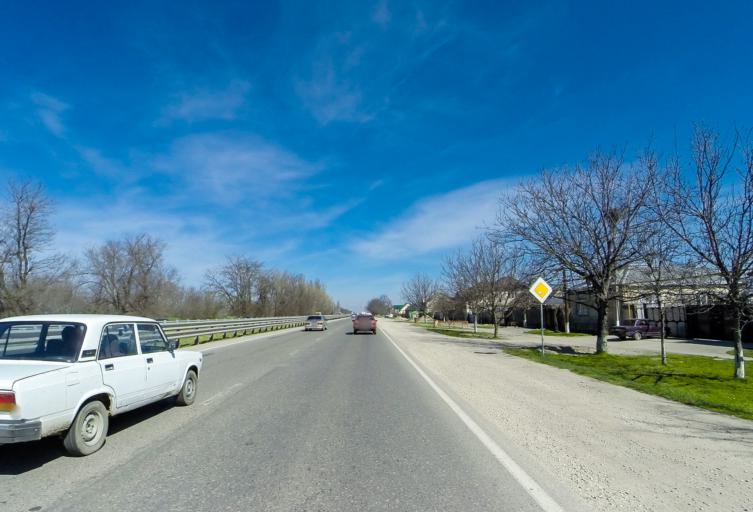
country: RU
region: Kabardino-Balkariya
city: Chegem Vtoroy
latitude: 43.5830
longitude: 43.5805
